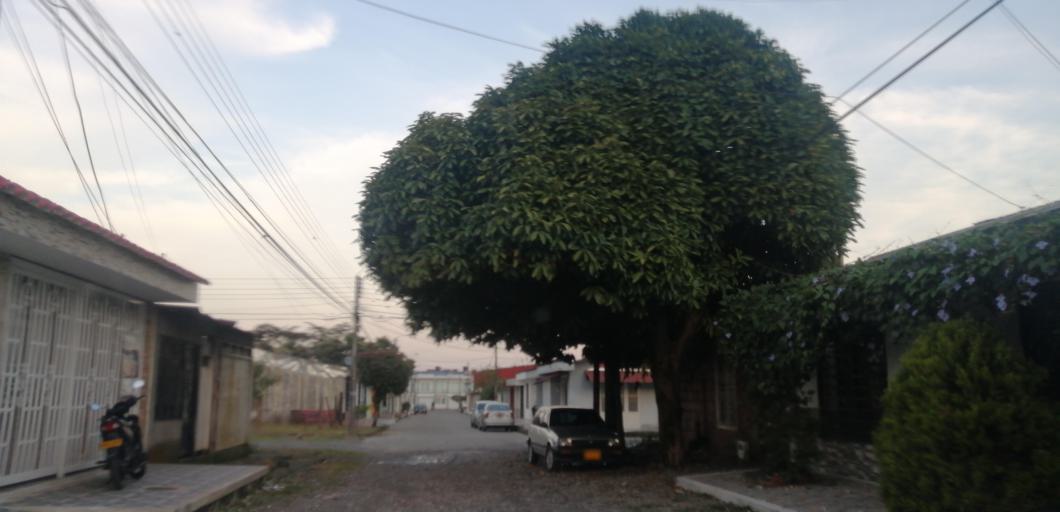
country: CO
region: Meta
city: Acacias
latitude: 3.9958
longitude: -73.7578
